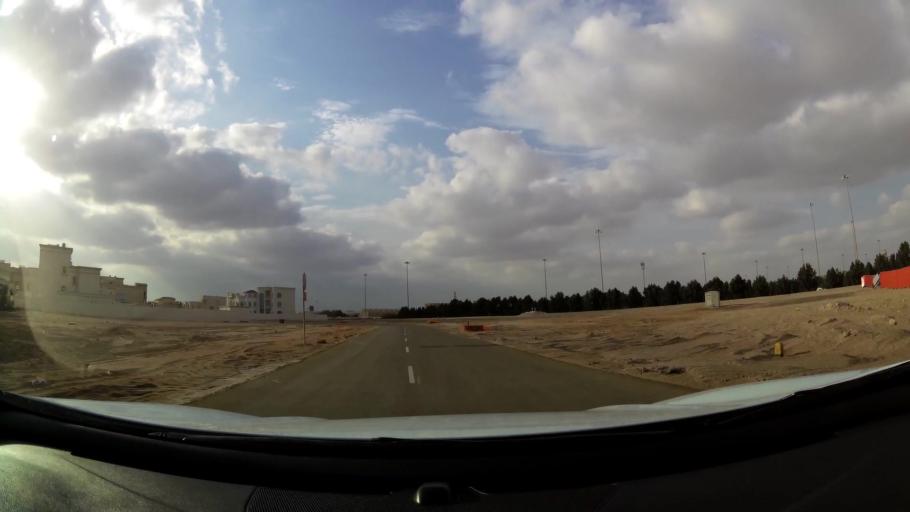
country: AE
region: Abu Dhabi
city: Abu Dhabi
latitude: 24.3730
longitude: 54.5495
